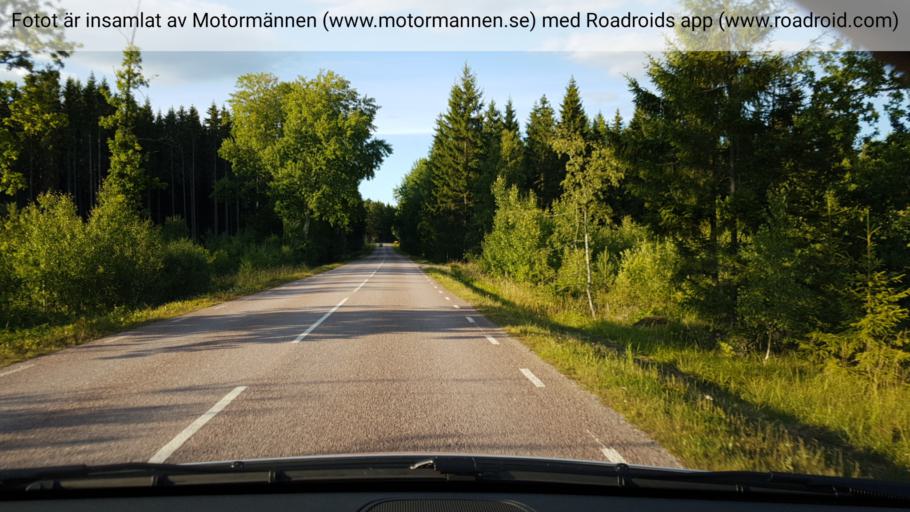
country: SE
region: Vaestmanland
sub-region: Vasteras
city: Tillberga
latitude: 59.7263
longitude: 16.6733
